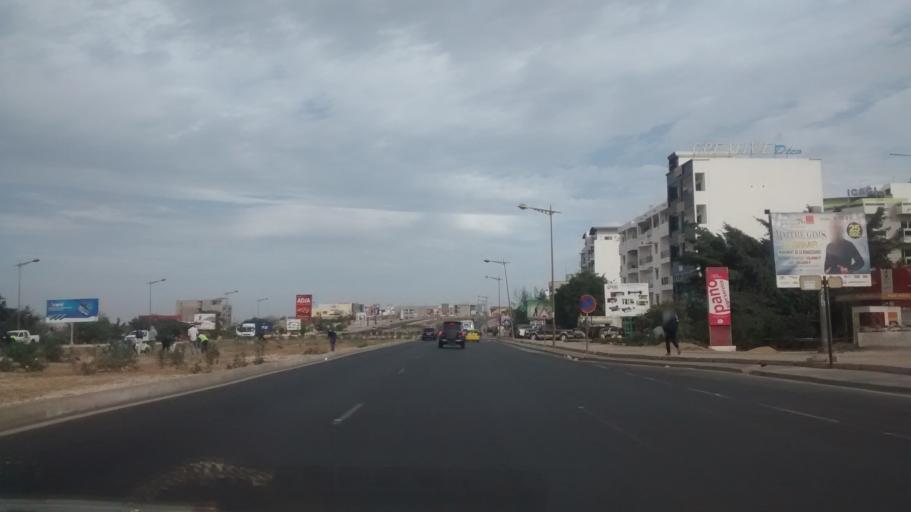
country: SN
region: Dakar
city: Mermoz Boabab
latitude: 14.7278
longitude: -17.4719
